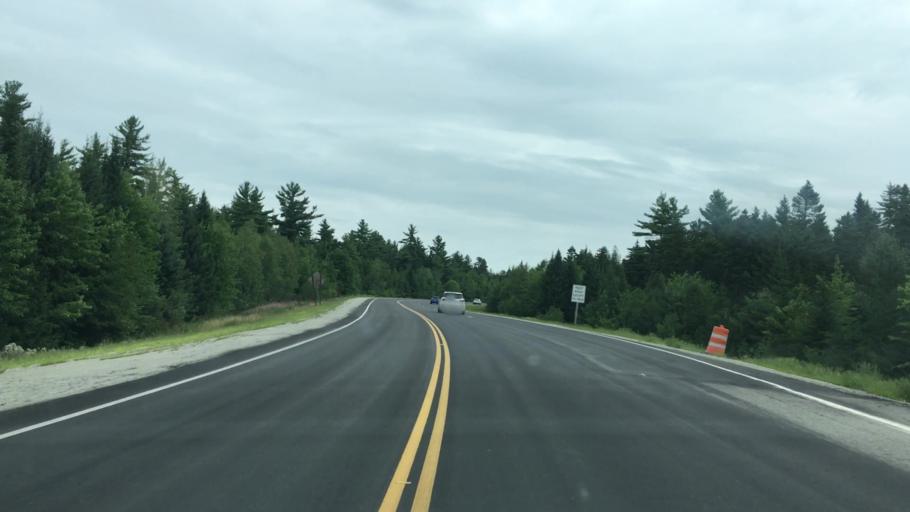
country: US
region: Maine
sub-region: Washington County
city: Addison
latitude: 44.9080
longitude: -67.8014
